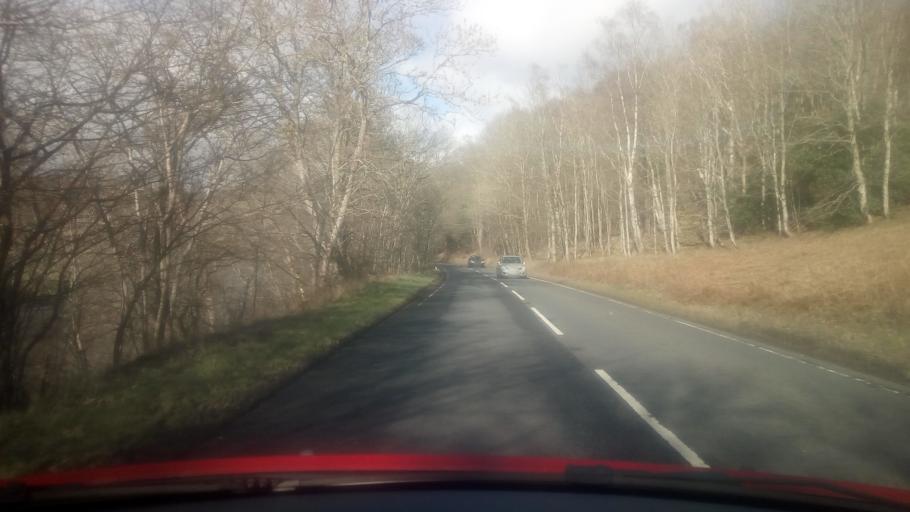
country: GB
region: Scotland
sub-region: The Scottish Borders
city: Selkirk
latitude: 55.6114
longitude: -2.9085
